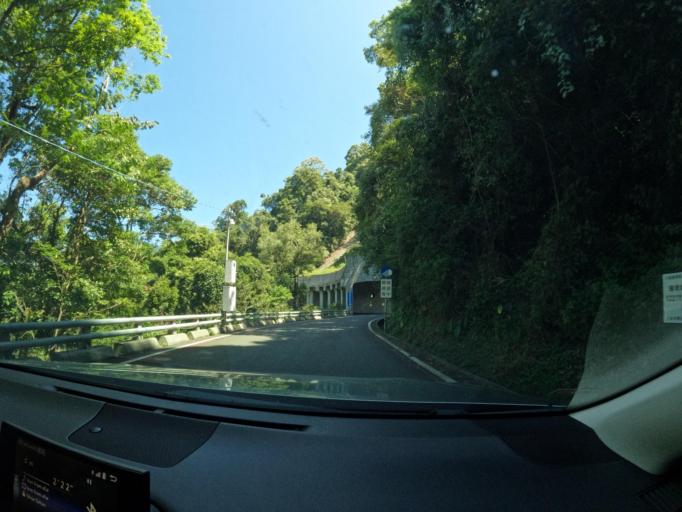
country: TW
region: Taiwan
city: Yujing
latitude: 23.2851
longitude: 120.8482
